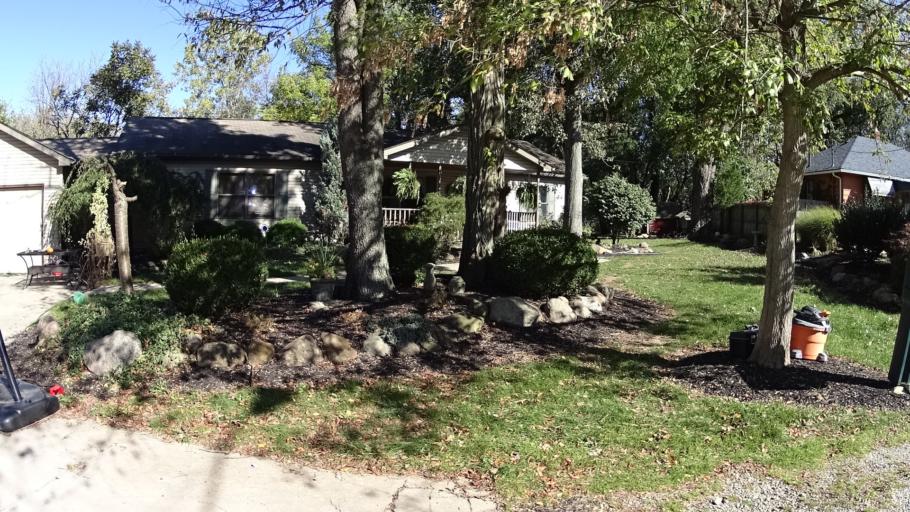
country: US
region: Ohio
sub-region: Lorain County
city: Lorain
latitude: 41.4201
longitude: -82.1559
